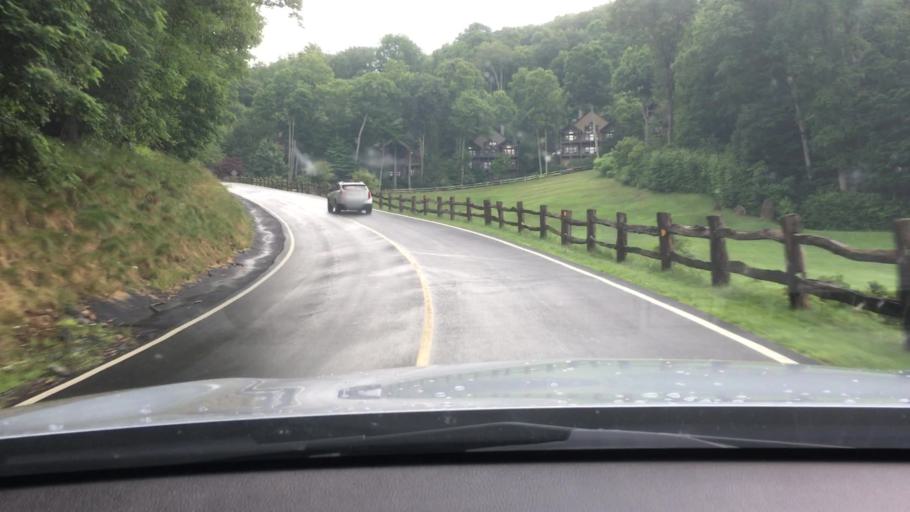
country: US
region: North Carolina
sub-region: Yancey County
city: Burnsville
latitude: 35.8786
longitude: -82.3477
